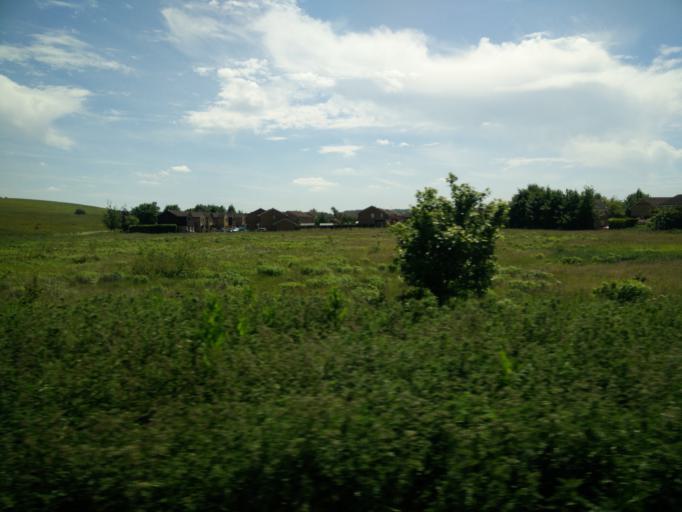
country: GB
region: England
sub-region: Hertfordshire
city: Baldock
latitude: 51.9936
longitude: -0.1706
